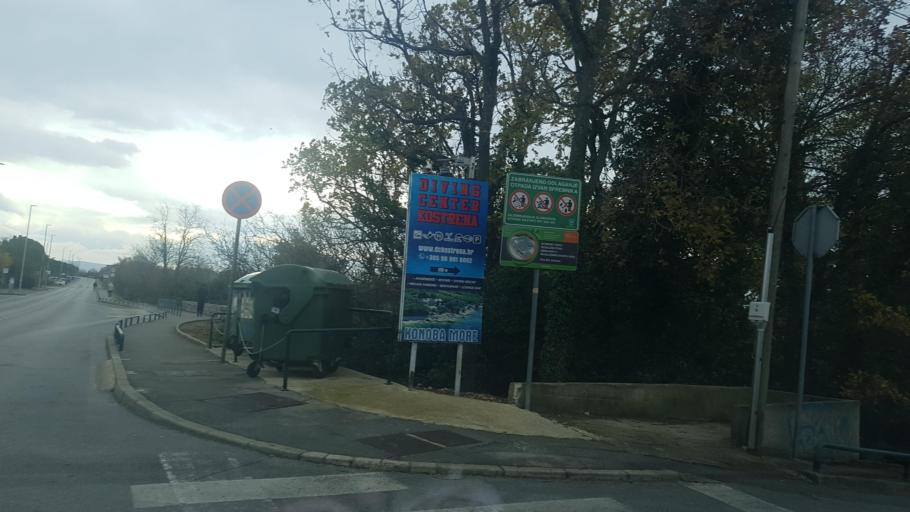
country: HR
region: Primorsko-Goranska
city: Skrljevo
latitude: 45.3040
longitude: 14.4902
